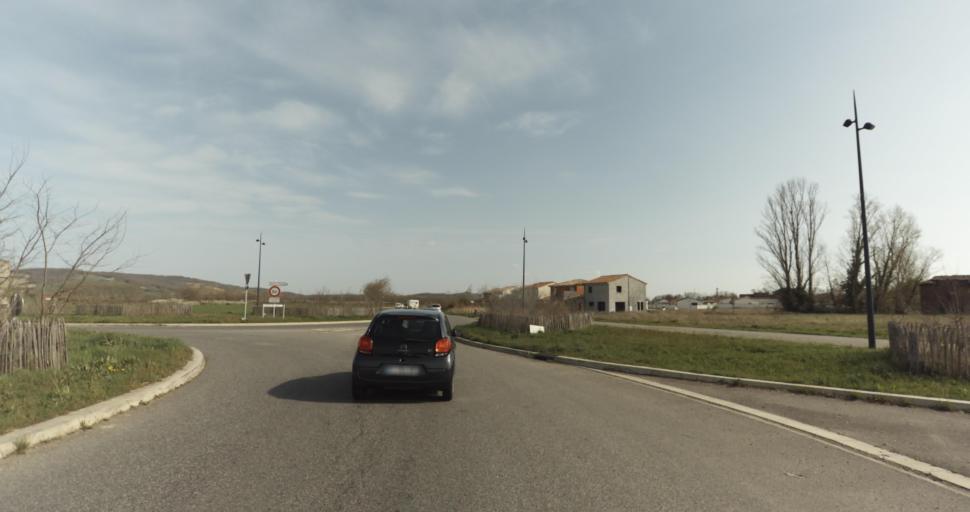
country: FR
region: Midi-Pyrenees
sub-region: Departement de la Haute-Garonne
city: Buzet-sur-Tarn
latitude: 43.7634
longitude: 1.6576
